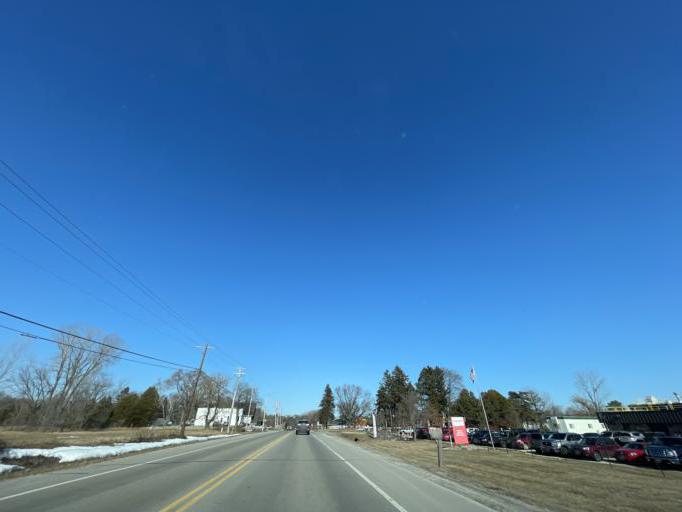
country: US
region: Wisconsin
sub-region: Brown County
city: Suamico
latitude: 44.6289
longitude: -88.0572
